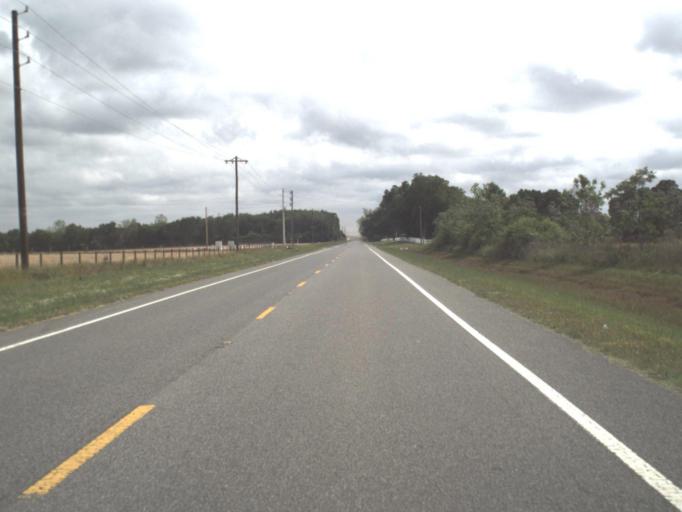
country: US
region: Florida
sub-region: Santa Rosa County
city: Point Baker
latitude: 30.7652
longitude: -87.0930
